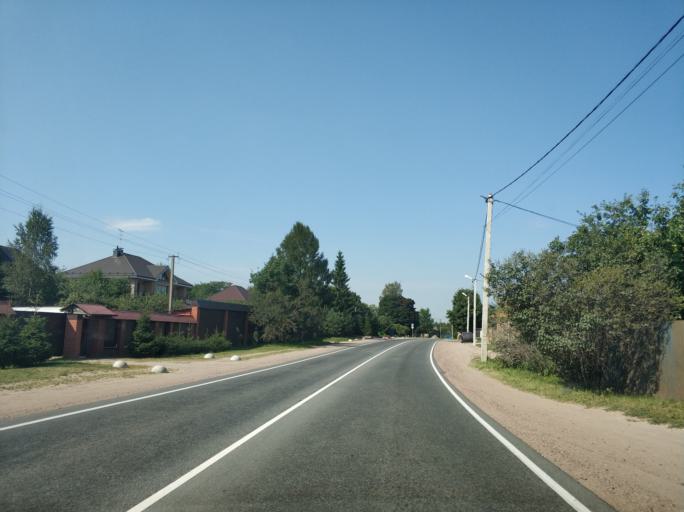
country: RU
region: Leningrad
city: Romanovka
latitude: 60.0495
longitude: 30.7170
